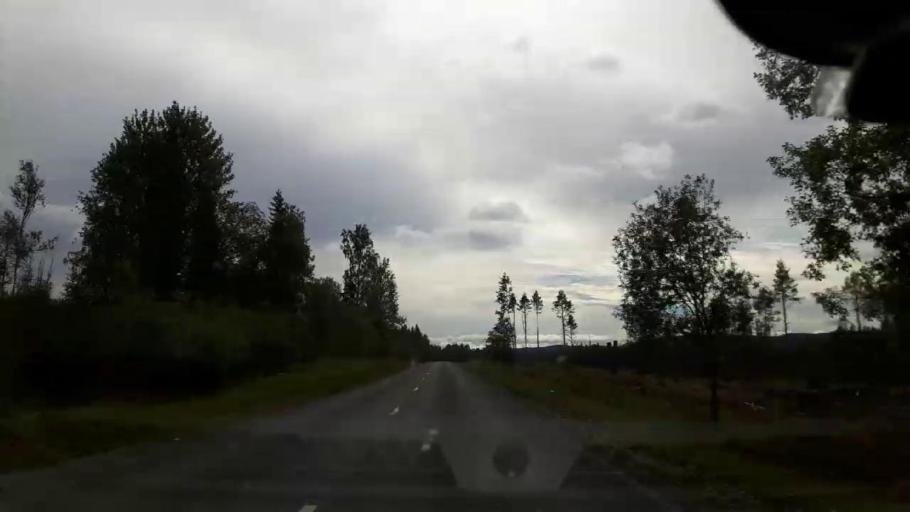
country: SE
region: Jaemtland
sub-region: Ragunda Kommun
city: Hammarstrand
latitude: 63.1078
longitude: 15.9107
